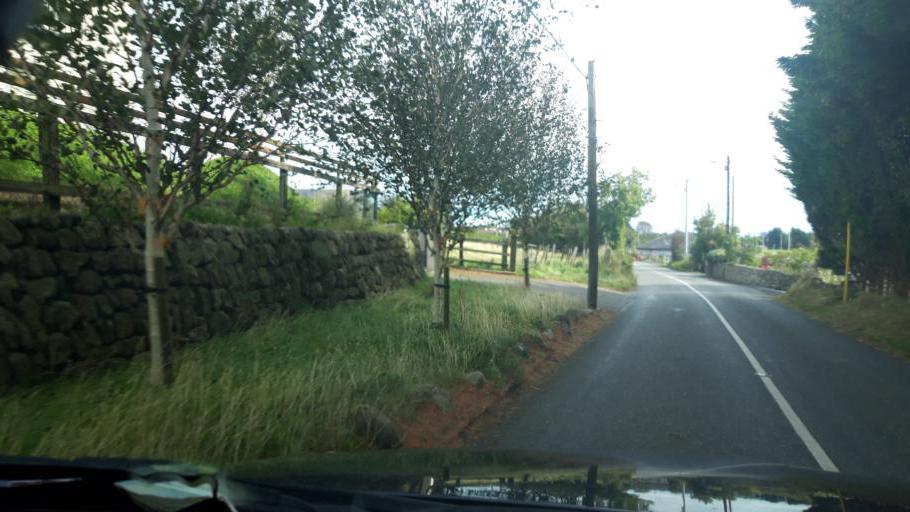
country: IE
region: Leinster
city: Sandyford
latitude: 53.2205
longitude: -6.2307
